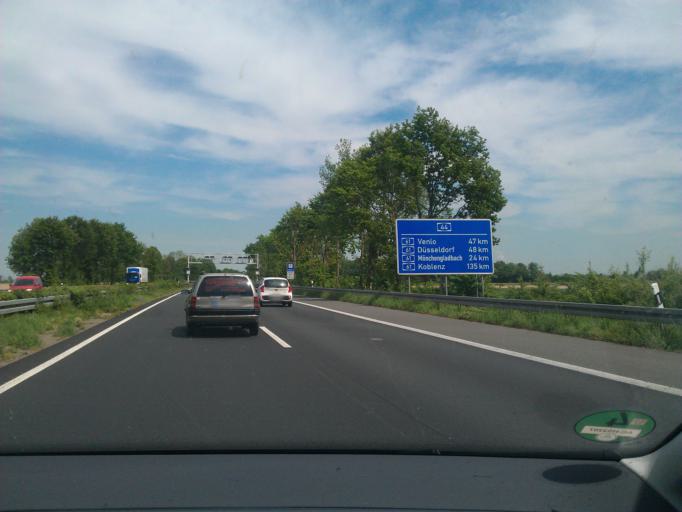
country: DE
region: North Rhine-Westphalia
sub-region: Regierungsbezirk Koln
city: Titz
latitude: 51.0129
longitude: 6.4148
